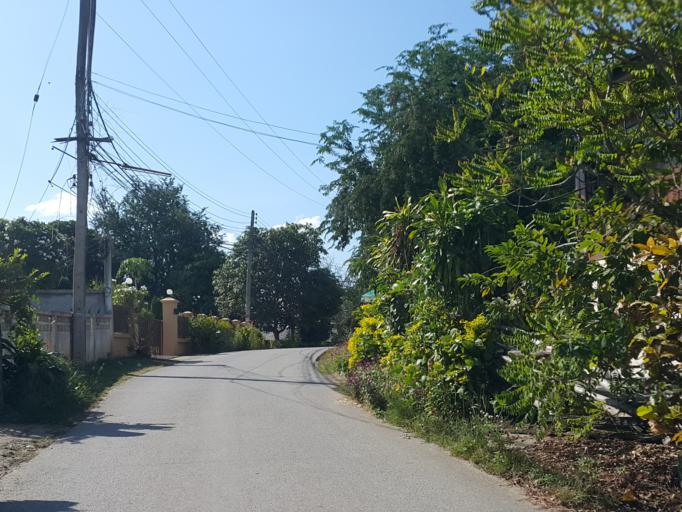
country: TH
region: Chiang Mai
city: San Sai
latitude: 18.9453
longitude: 98.9193
